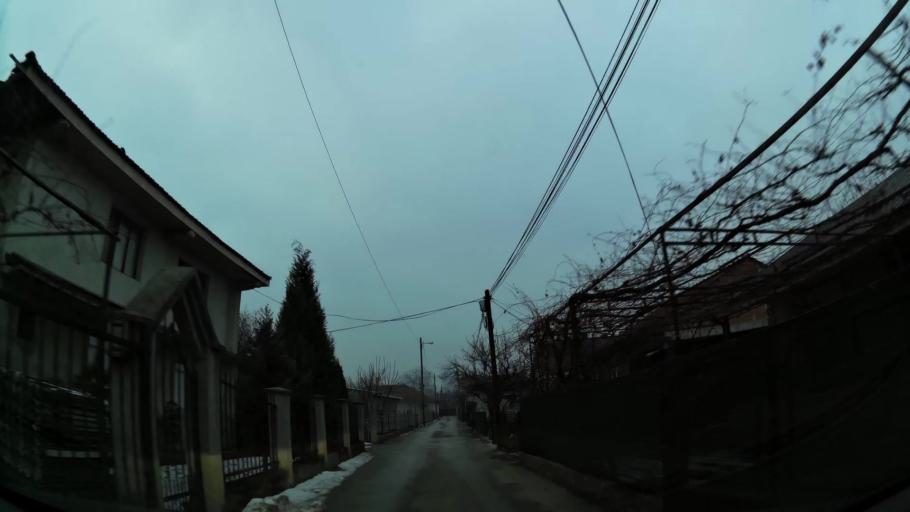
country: MK
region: Kisela Voda
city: Usje
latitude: 41.9695
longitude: 21.4762
